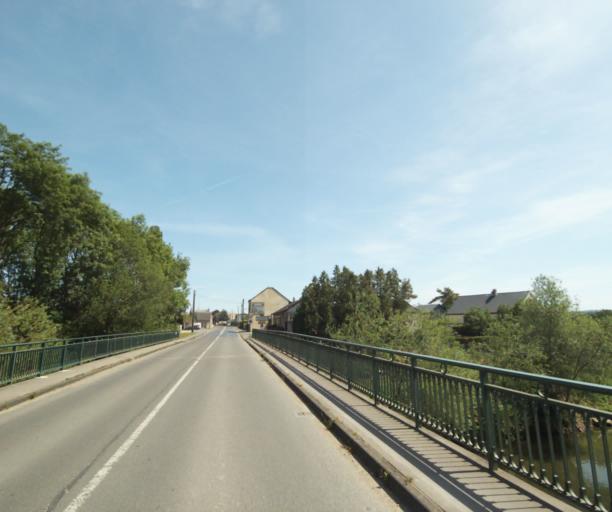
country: FR
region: Champagne-Ardenne
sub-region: Departement des Ardennes
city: Warcq
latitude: 49.7685
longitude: 4.6818
